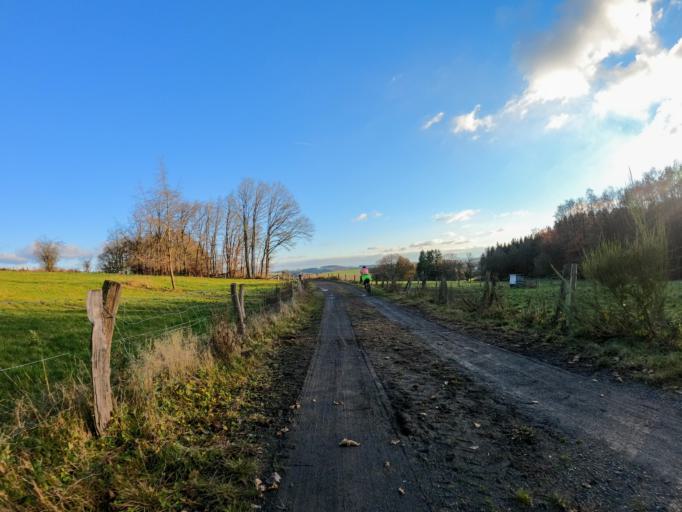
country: LU
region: Diekirch
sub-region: Canton de Wiltz
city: Bavigne
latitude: 49.9713
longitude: 5.8308
